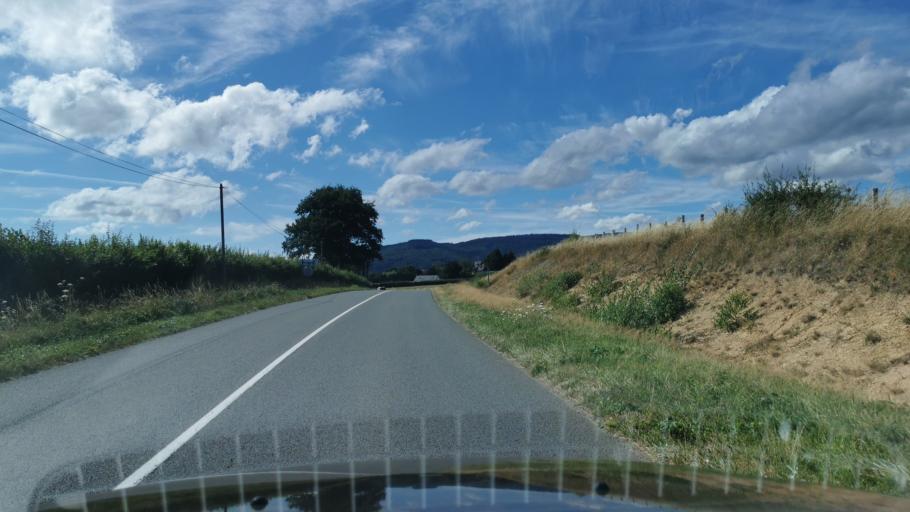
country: FR
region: Bourgogne
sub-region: Departement de Saone-et-Loire
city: Marmagne
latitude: 46.8531
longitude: 4.3218
